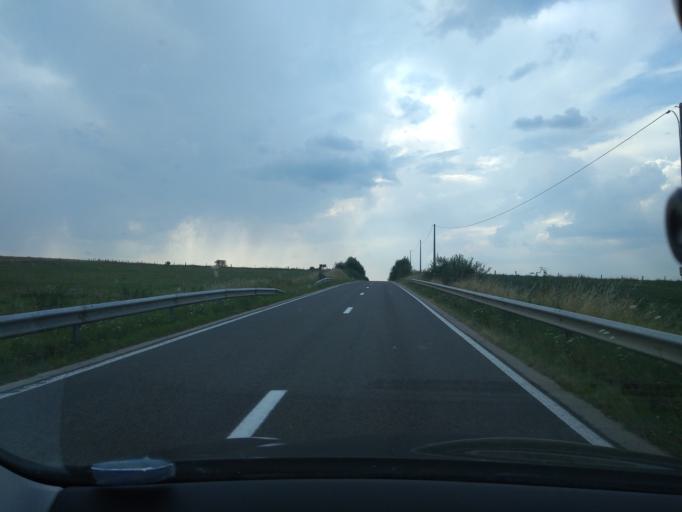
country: BE
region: Wallonia
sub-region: Province du Luxembourg
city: Bertogne
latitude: 50.0806
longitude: 5.6822
